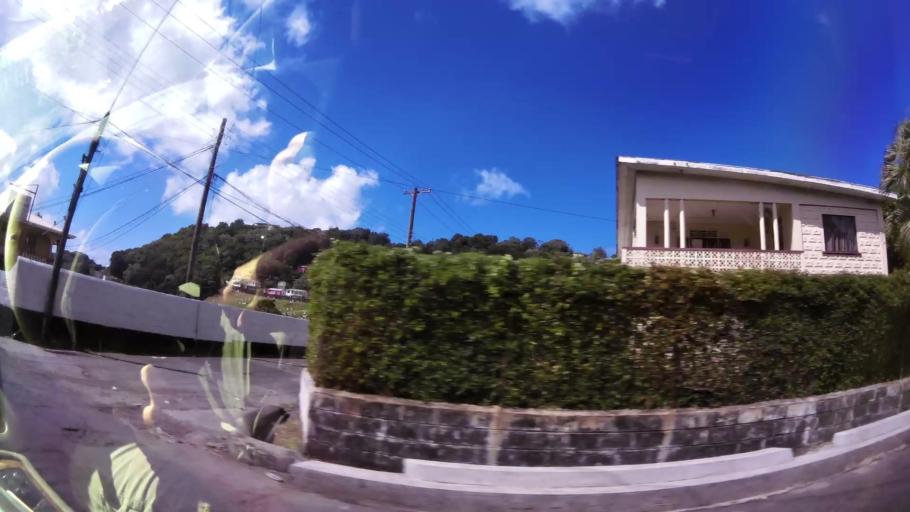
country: VC
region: Saint George
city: Kingstown Park
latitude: 13.1599
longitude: -61.2302
